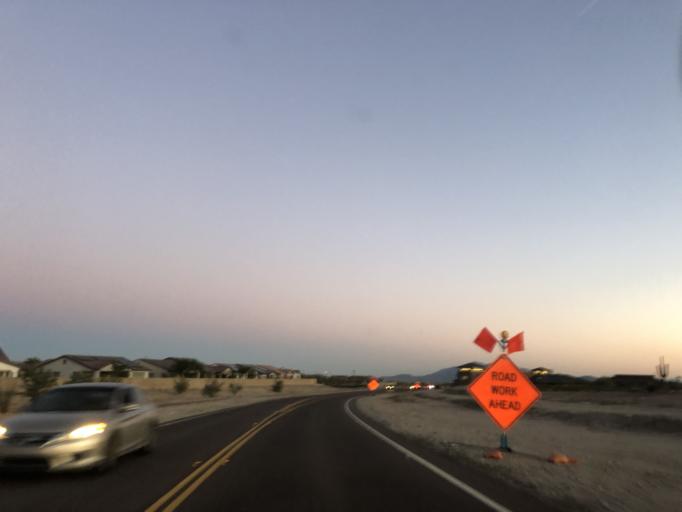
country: US
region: Arizona
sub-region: Maricopa County
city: Citrus Park
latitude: 33.5012
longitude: -112.5056
